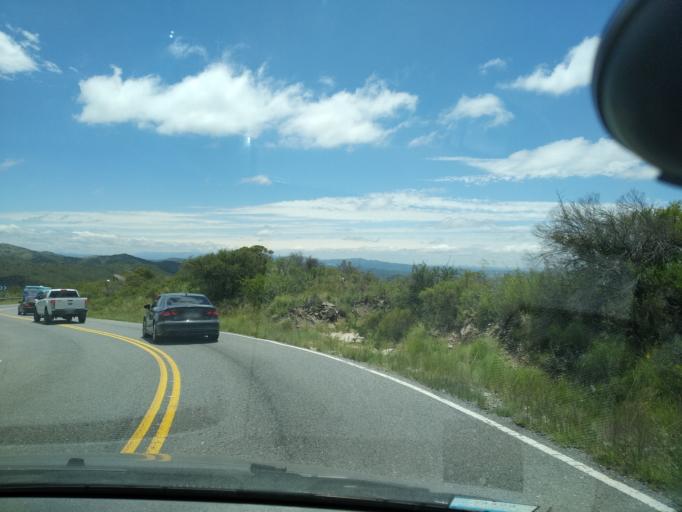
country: AR
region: Cordoba
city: Cuesta Blanca
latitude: -31.5927
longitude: -64.5273
